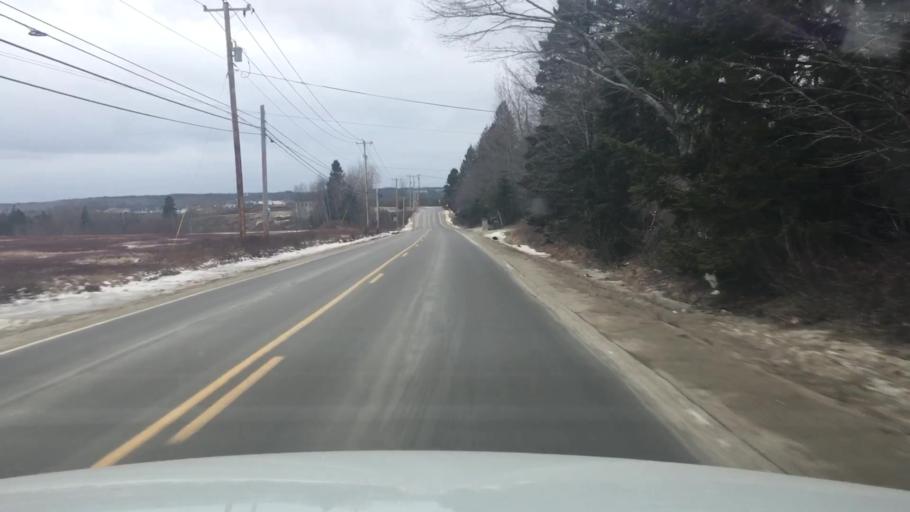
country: US
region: Maine
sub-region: Washington County
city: Addison
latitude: 44.6211
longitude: -67.7067
